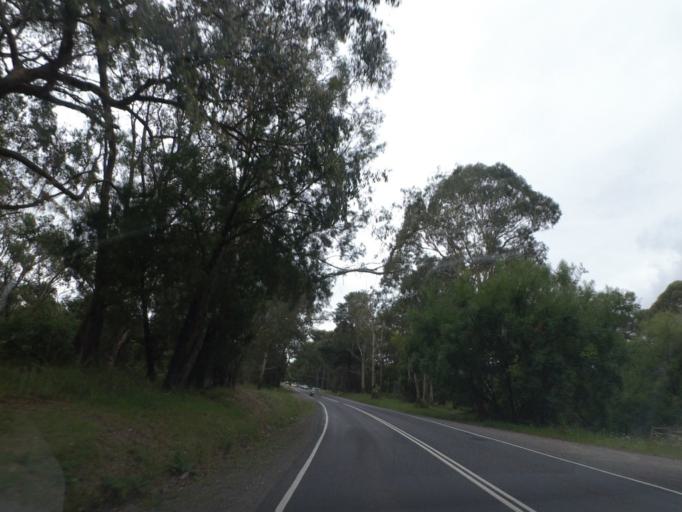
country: AU
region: Victoria
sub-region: Yarra Ranges
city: Mount Evelyn
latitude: -37.7953
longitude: 145.3760
